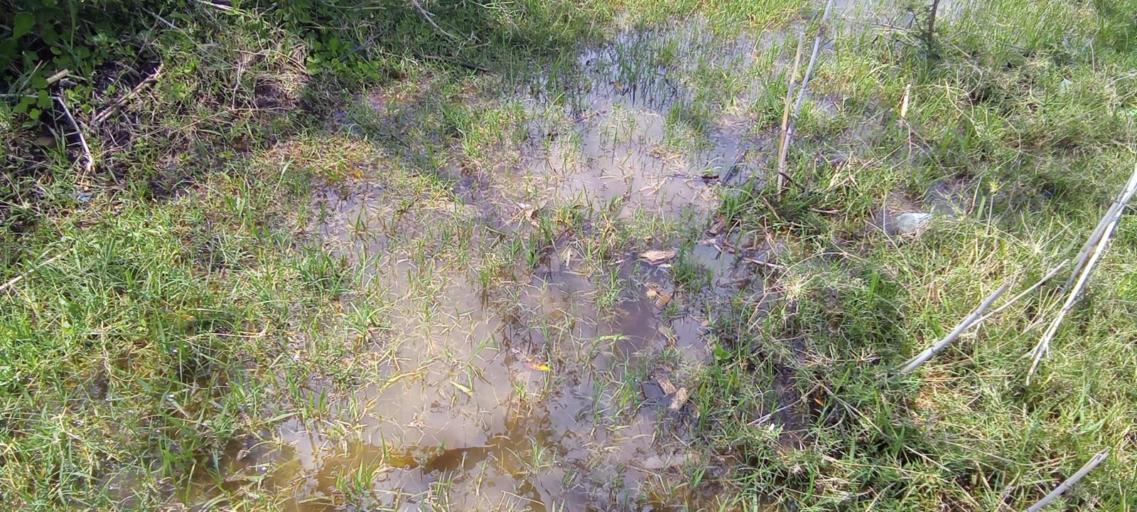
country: KE
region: Homa Bay
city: Homa Bay
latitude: -0.4635
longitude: 34.1838
